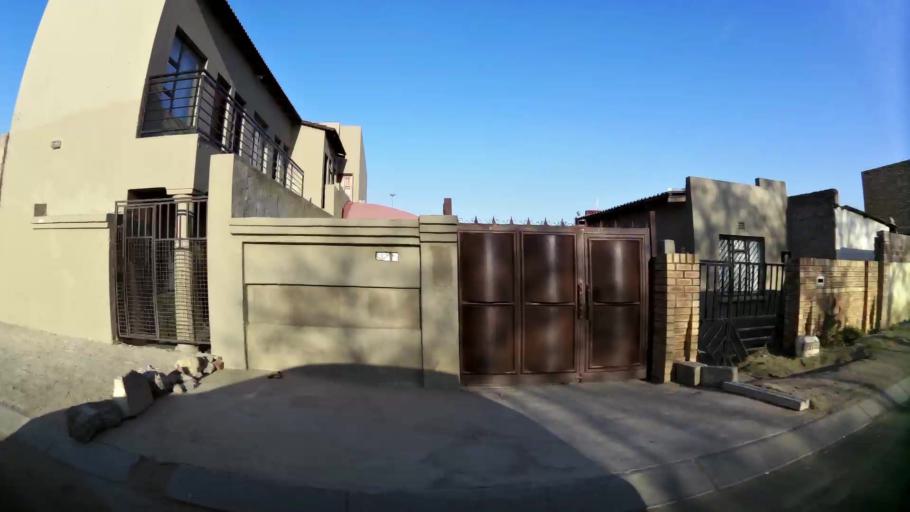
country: ZA
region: Gauteng
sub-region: City of Johannesburg Metropolitan Municipality
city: Soweto
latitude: -26.2542
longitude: 27.8804
